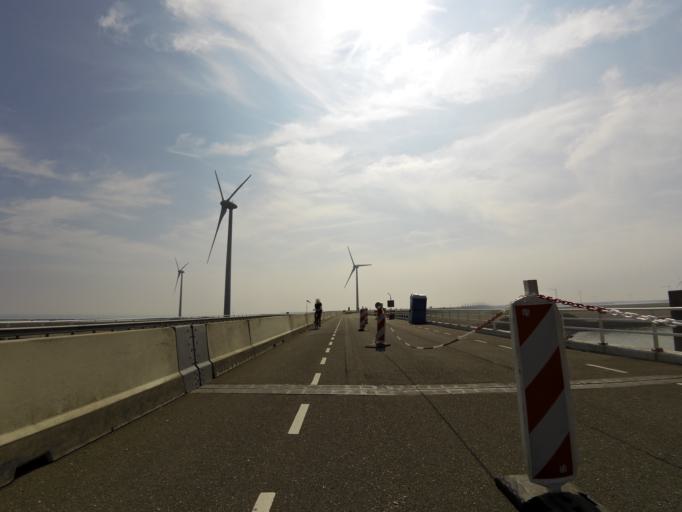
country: NL
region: Zeeland
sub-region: Schouwen-Duiveland
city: Burgh
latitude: 51.6566
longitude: 3.7229
